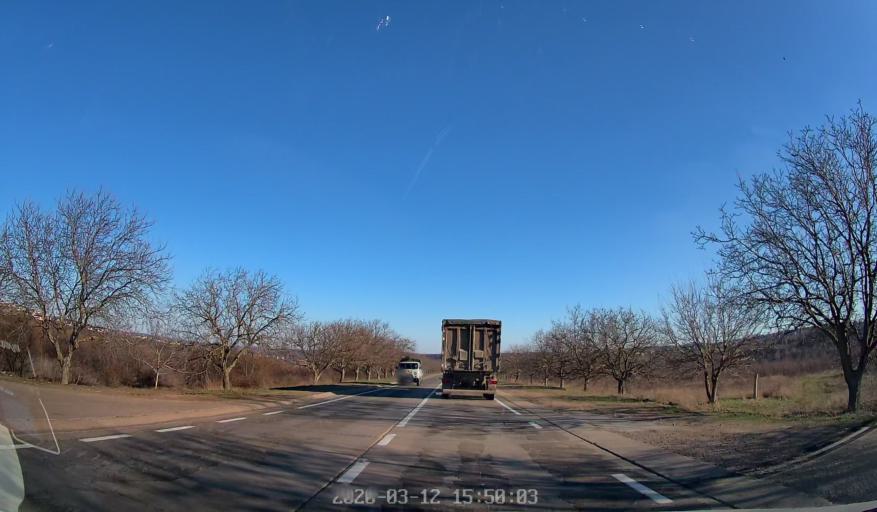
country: MD
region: Chisinau
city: Ciorescu
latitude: 47.0764
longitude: 28.9504
